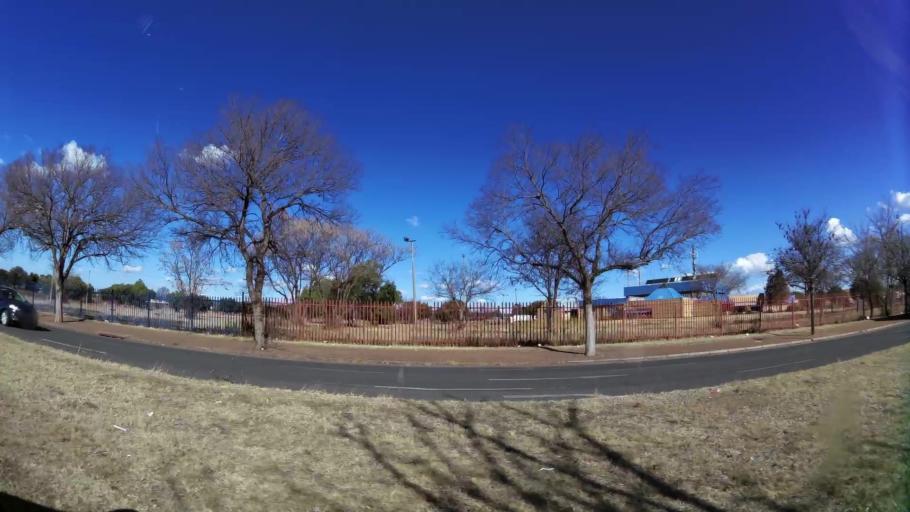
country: ZA
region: Gauteng
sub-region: West Rand District Municipality
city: Carletonville
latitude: -26.3591
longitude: 27.3836
